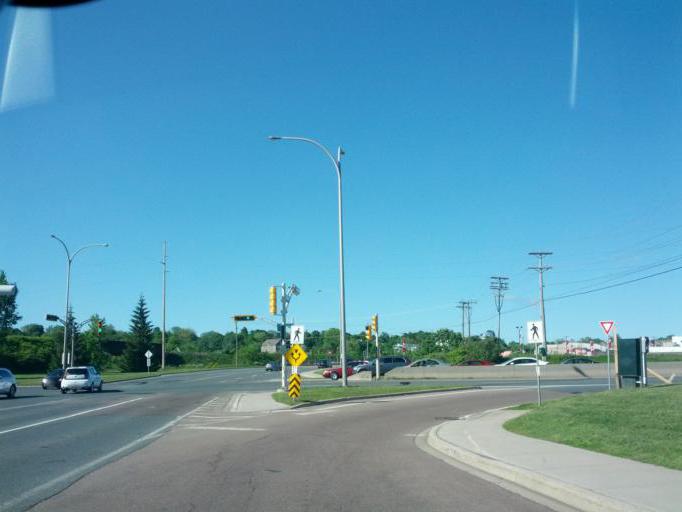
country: CA
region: New Brunswick
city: Moncton
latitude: 46.0981
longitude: -64.7769
